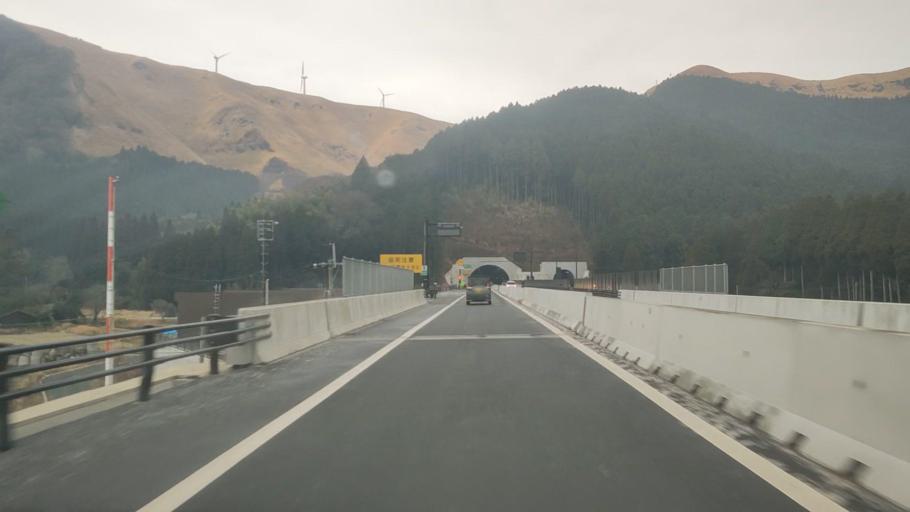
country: JP
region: Kumamoto
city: Aso
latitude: 32.9139
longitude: 130.9779
